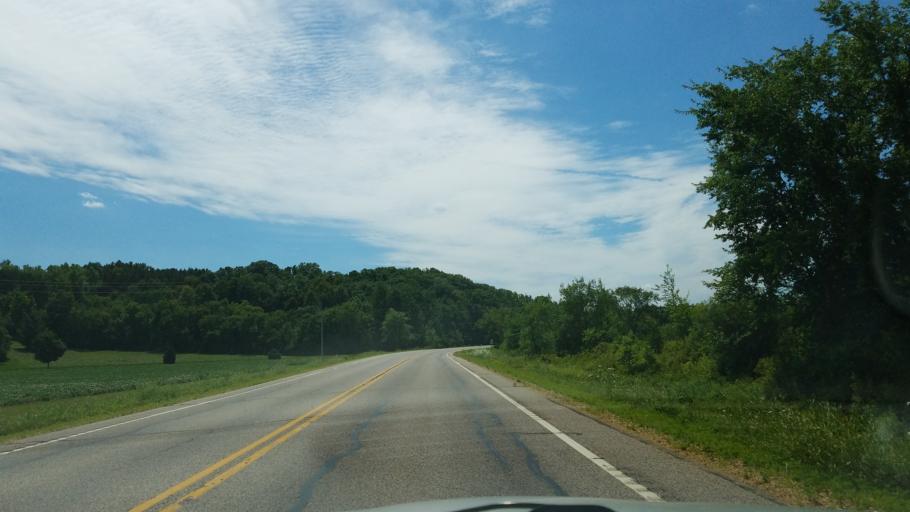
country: US
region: Wisconsin
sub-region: Saint Croix County
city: Glenwood City
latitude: 45.0346
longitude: -92.1840
